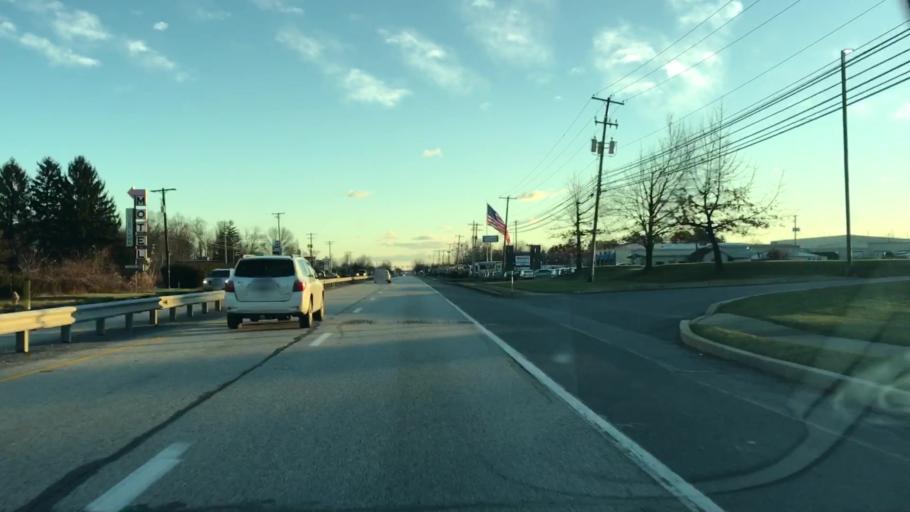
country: US
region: Pennsylvania
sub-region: Dauphin County
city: Skyline View
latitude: 40.3335
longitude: -76.7363
